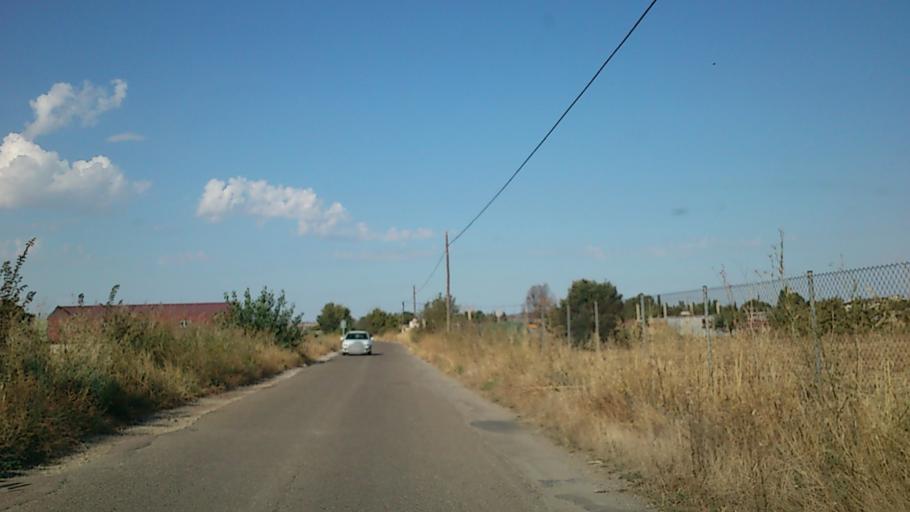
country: ES
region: Aragon
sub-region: Provincia de Zaragoza
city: Villanueva de Gallego
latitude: 41.7323
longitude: -0.8014
